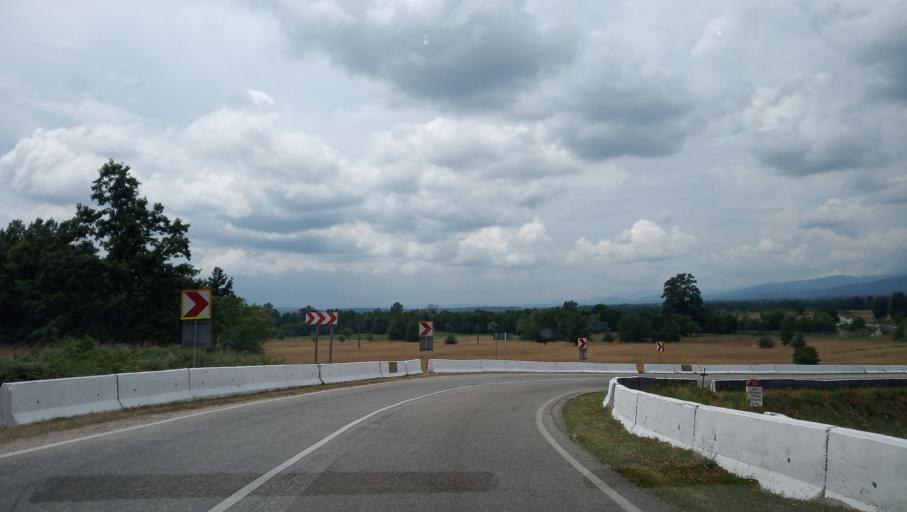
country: RO
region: Gorj
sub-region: Comuna Runcu
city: Valea Mare
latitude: 45.0867
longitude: 23.0967
